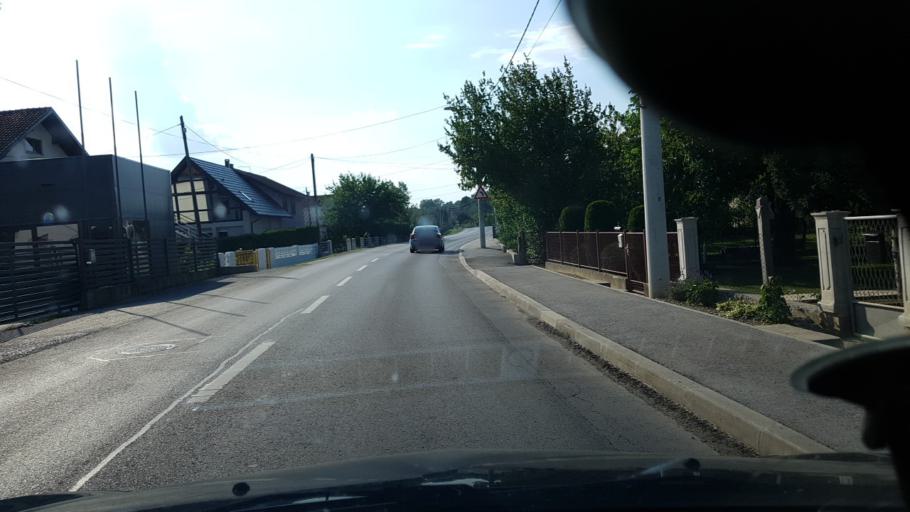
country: HR
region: Zagrebacka
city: Bregana
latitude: 45.8839
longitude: 15.7142
